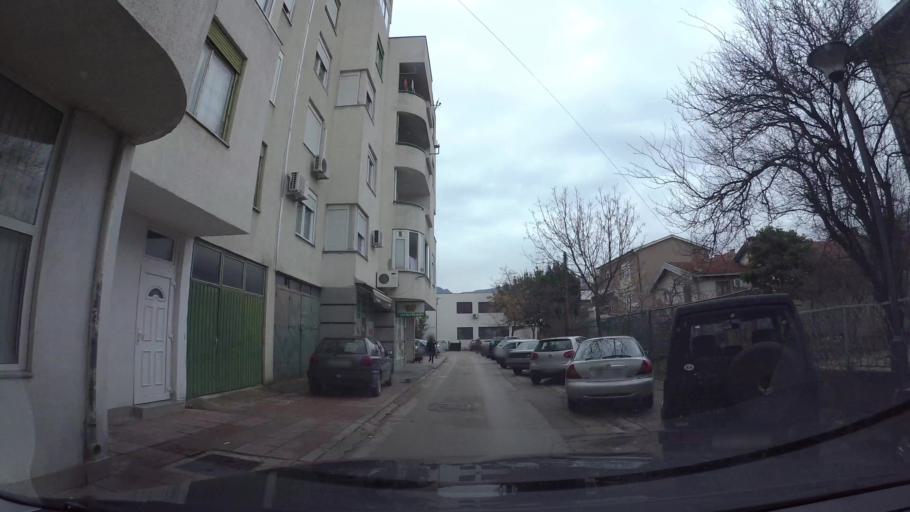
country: BA
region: Federation of Bosnia and Herzegovina
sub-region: Hercegovacko-Bosanski Kanton
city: Mostar
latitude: 43.3413
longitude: 17.8094
